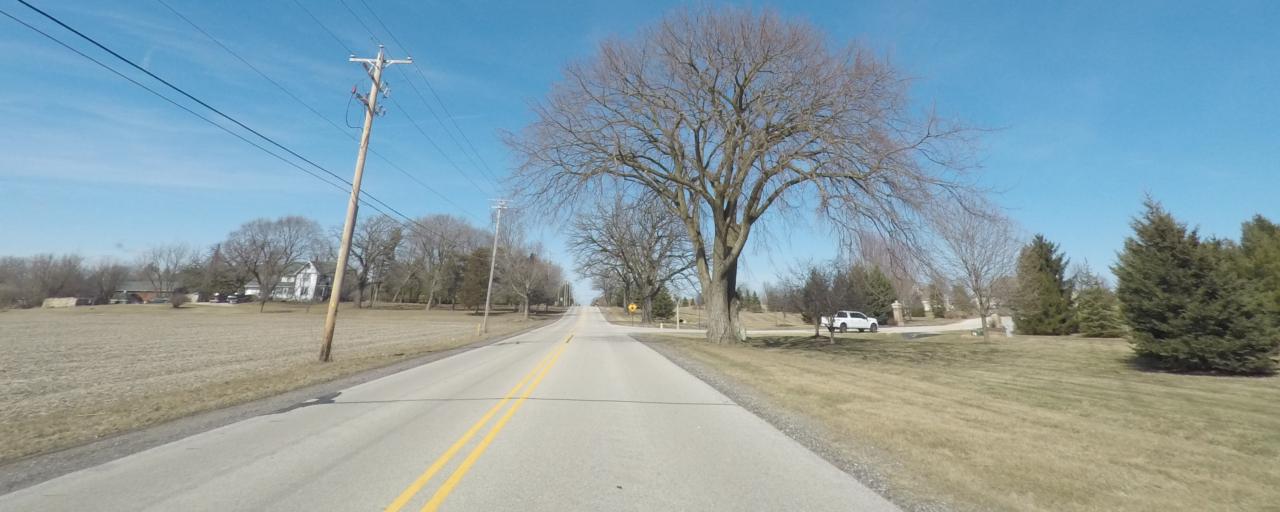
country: US
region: Wisconsin
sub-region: Waukesha County
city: Hartland
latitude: 43.1276
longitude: -88.3275
